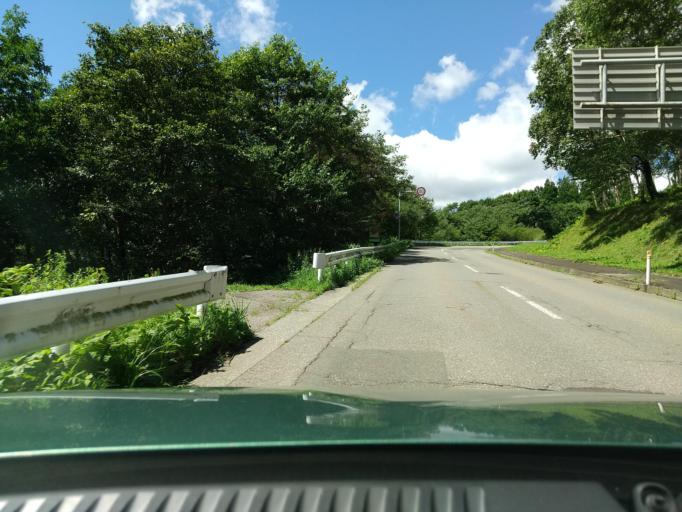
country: JP
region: Iwate
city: Shizukuishi
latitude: 39.7657
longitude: 140.7586
